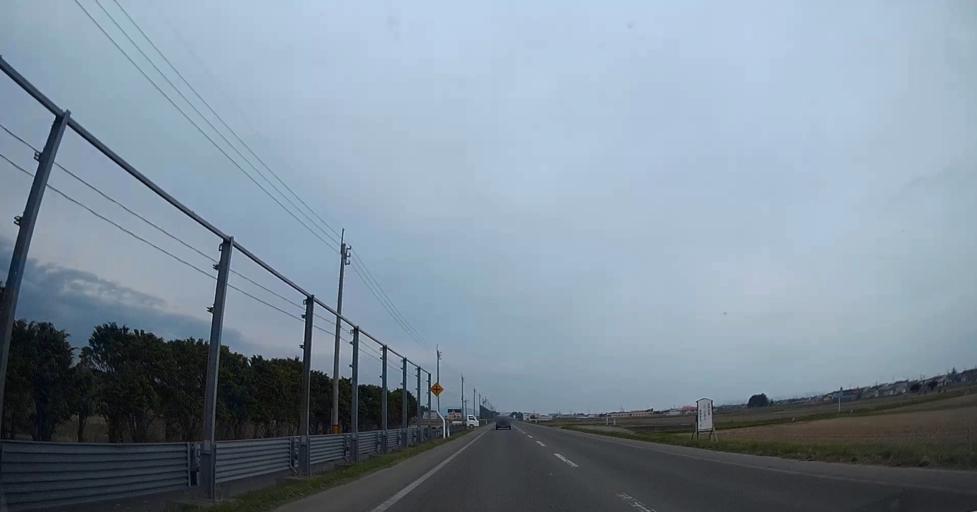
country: JP
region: Aomori
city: Aomori Shi
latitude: 40.8839
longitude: 140.6701
